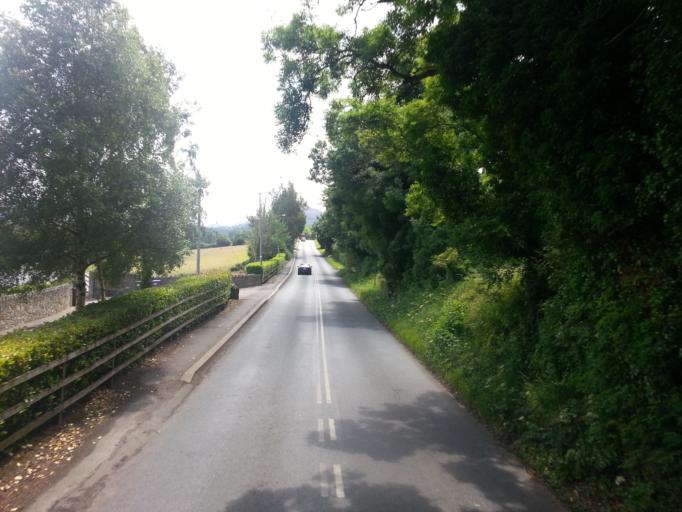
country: IE
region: Leinster
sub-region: Wicklow
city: Enniskerry
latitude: 53.2115
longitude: -6.1757
